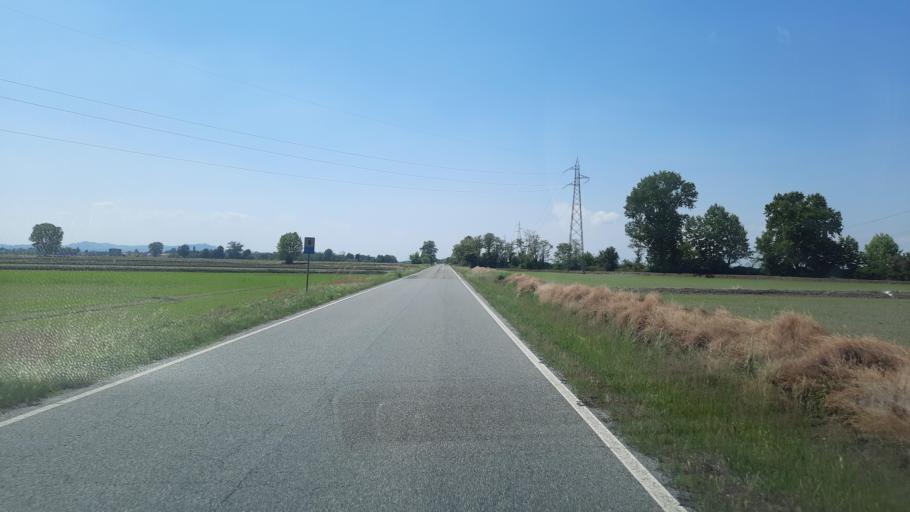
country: IT
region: Piedmont
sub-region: Provincia di Alessandria
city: Balzola
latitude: 45.1863
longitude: 8.4273
